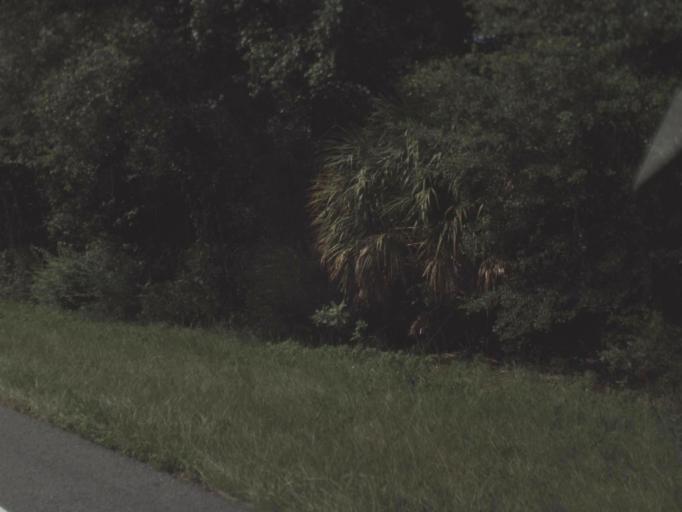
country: US
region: Florida
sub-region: Citrus County
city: Citrus Springs
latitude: 28.9872
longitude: -82.4358
